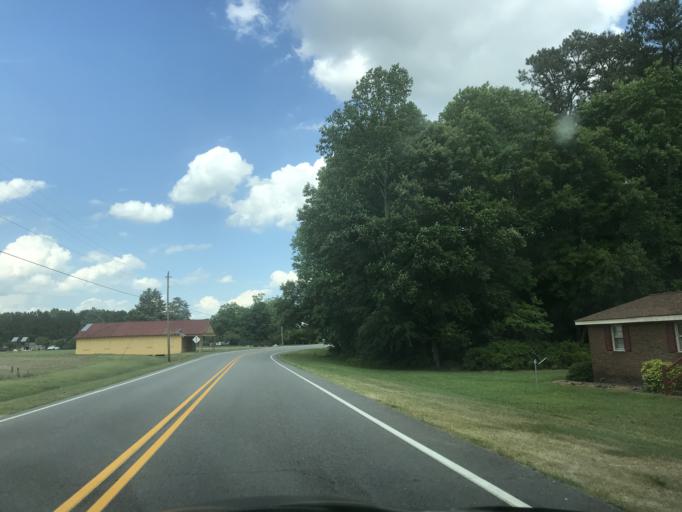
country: US
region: North Carolina
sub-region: Nash County
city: Spring Hope
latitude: 35.9620
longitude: -78.0609
